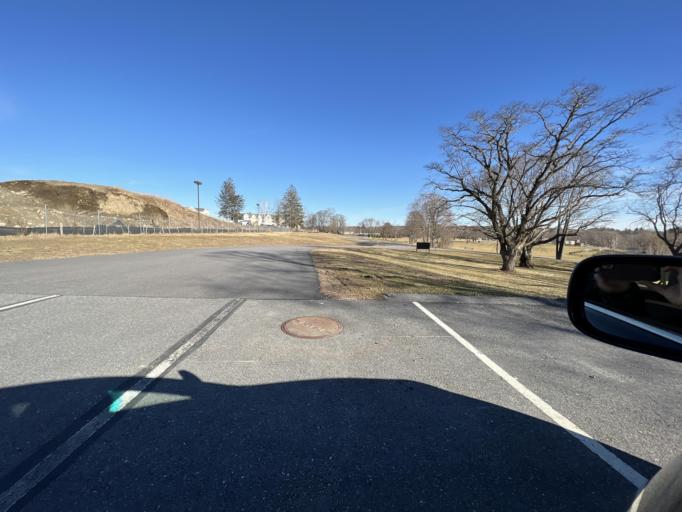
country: US
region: Massachusetts
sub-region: Worcester County
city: Westborough
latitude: 42.2996
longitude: -71.6092
